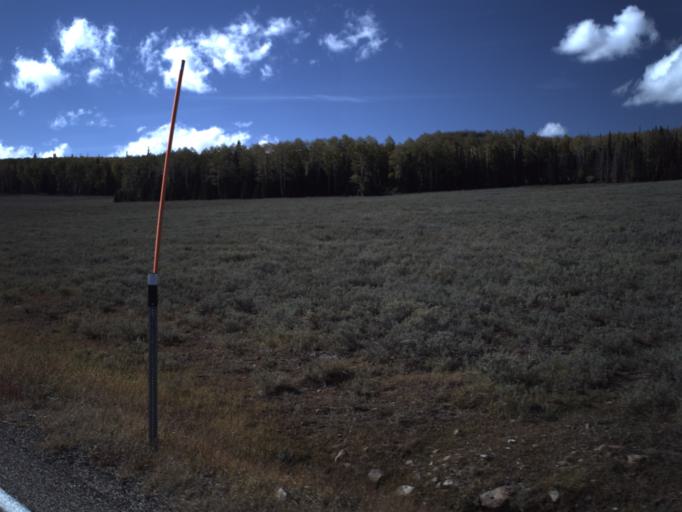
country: US
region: Utah
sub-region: Iron County
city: Parowan
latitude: 37.6539
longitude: -112.7738
